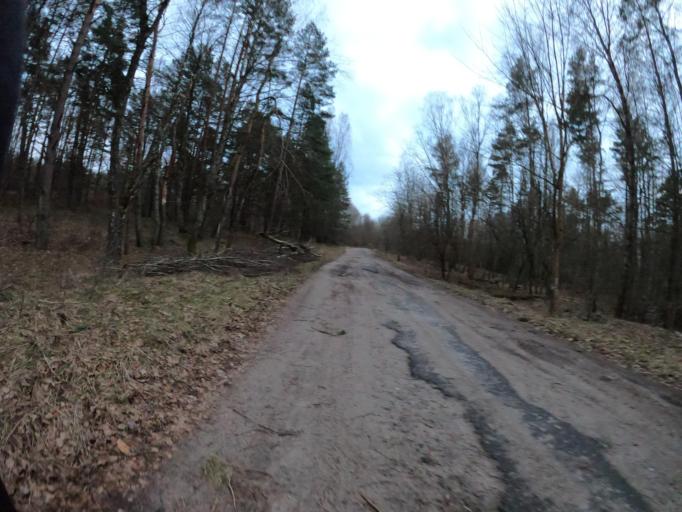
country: PL
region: West Pomeranian Voivodeship
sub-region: Powiat szczecinecki
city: Borne Sulinowo
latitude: 53.5449
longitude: 16.5842
